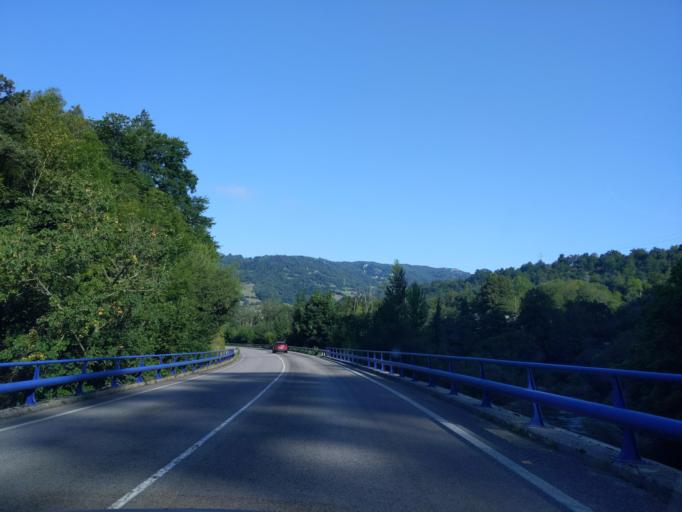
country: ES
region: Asturias
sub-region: Province of Asturias
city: Pola de Laviana
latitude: 43.2330
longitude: -5.4954
